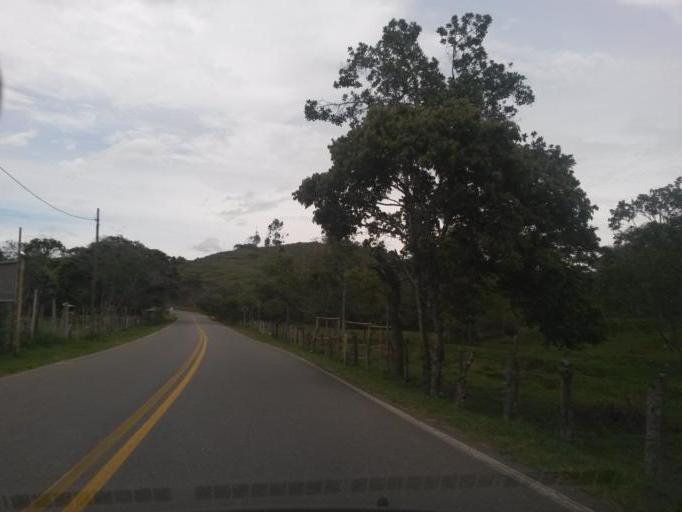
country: CO
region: Cauca
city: Lopez
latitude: 2.4337
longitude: -76.7614
